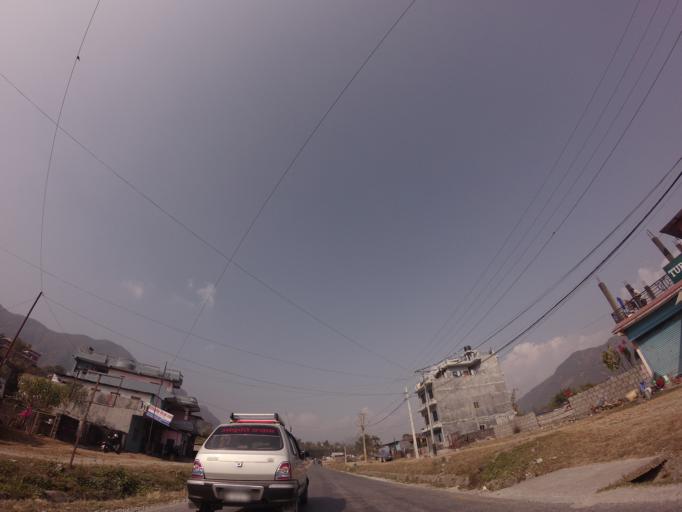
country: NP
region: Western Region
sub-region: Gandaki Zone
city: Pokhara
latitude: 28.2576
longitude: 83.9628
